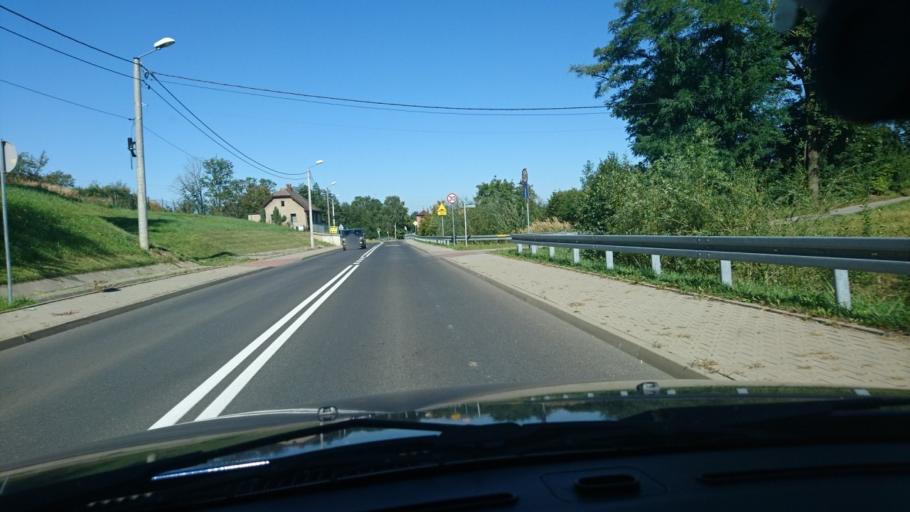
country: PL
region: Silesian Voivodeship
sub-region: Powiat bielski
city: Mazancowice
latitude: 49.8208
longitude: 18.9860
